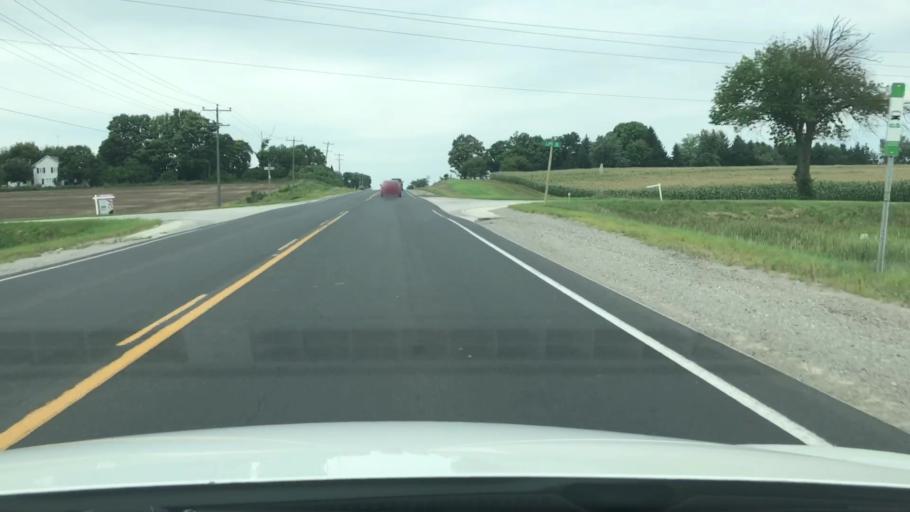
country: CA
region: Ontario
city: Bradford West Gwillimbury
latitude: 44.1875
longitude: -79.5826
